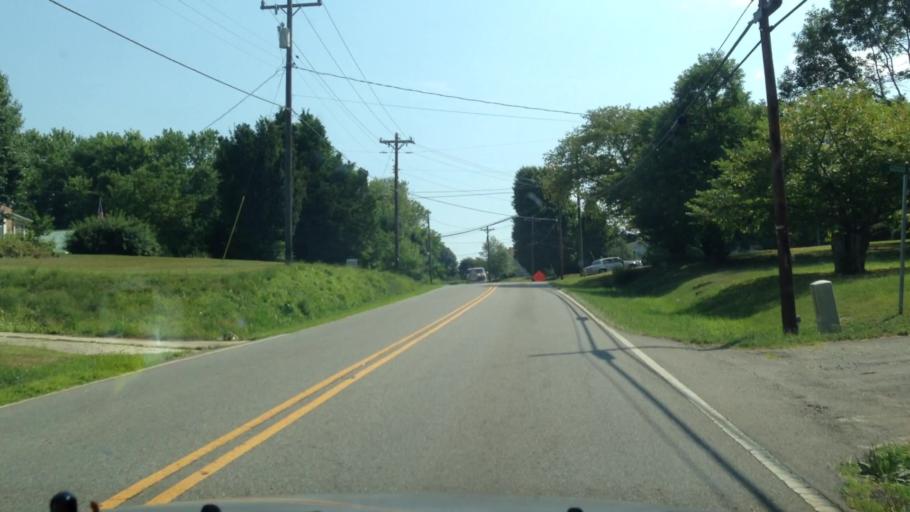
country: US
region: North Carolina
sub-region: Surry County
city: Flat Rock
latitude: 36.5064
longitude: -80.5769
